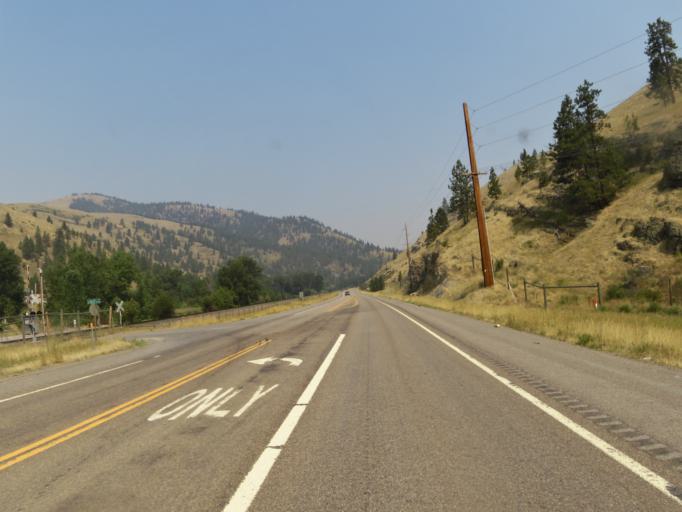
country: US
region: Montana
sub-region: Missoula County
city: Frenchtown
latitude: 47.2466
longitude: -114.1695
